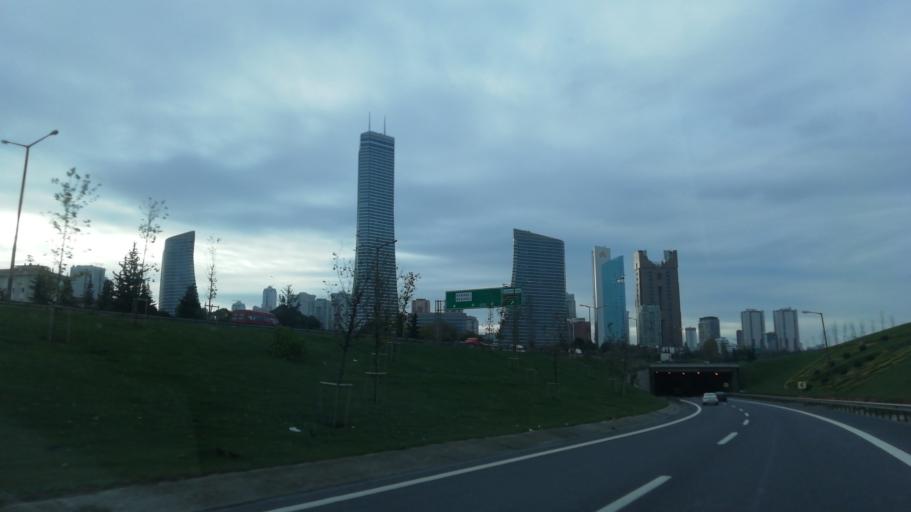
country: TR
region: Istanbul
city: Umraniye
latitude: 41.0018
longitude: 29.1194
